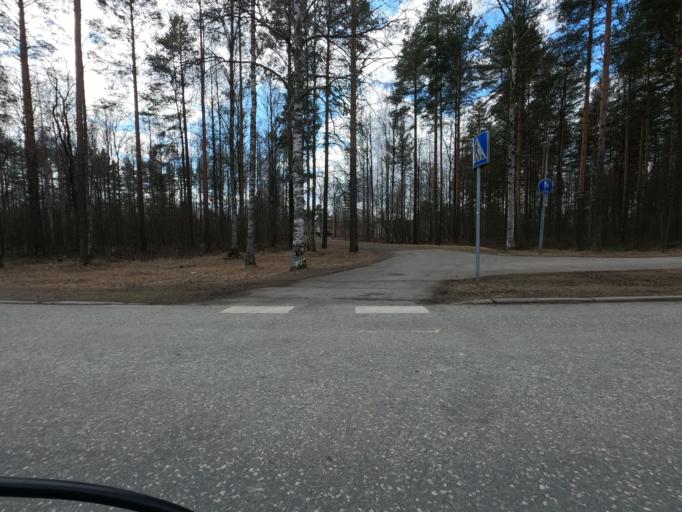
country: FI
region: North Karelia
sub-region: Joensuu
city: Joensuu
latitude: 62.6106
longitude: 29.7608
